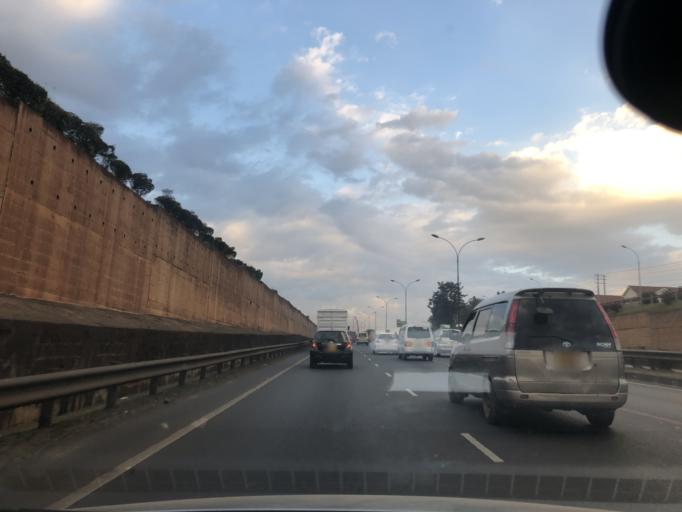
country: KE
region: Nairobi Area
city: Pumwani
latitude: -1.2336
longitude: 36.8744
